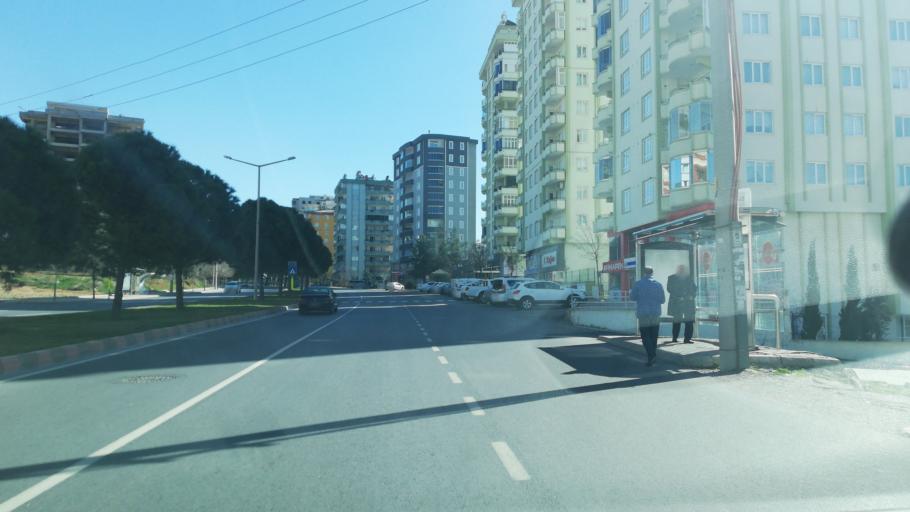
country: TR
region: Kahramanmaras
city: Kahramanmaras
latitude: 37.5829
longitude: 36.8804
